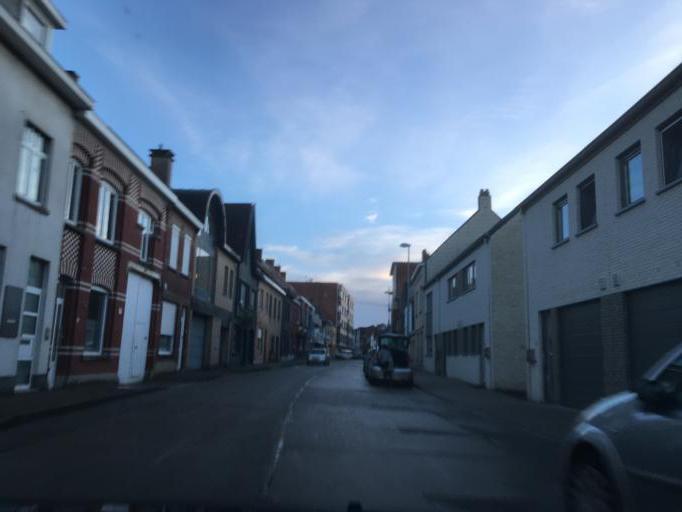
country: BE
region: Flanders
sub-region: Provincie West-Vlaanderen
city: Roeselare
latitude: 50.9528
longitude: 3.1193
